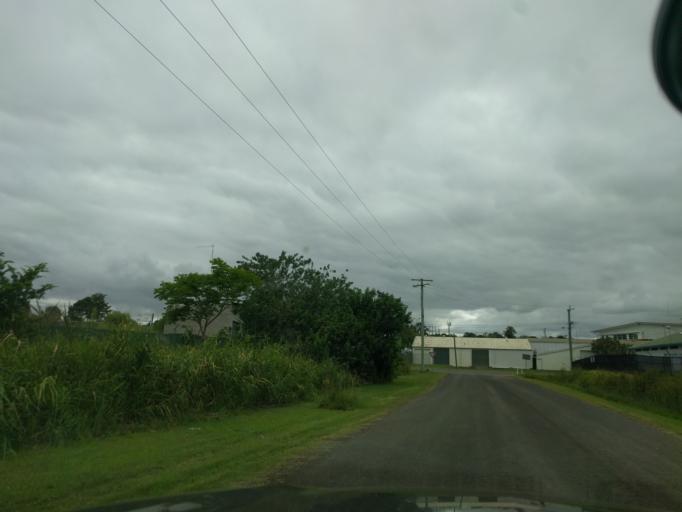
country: AU
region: Queensland
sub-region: Logan
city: Cedar Vale
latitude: -27.9862
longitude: 152.9935
